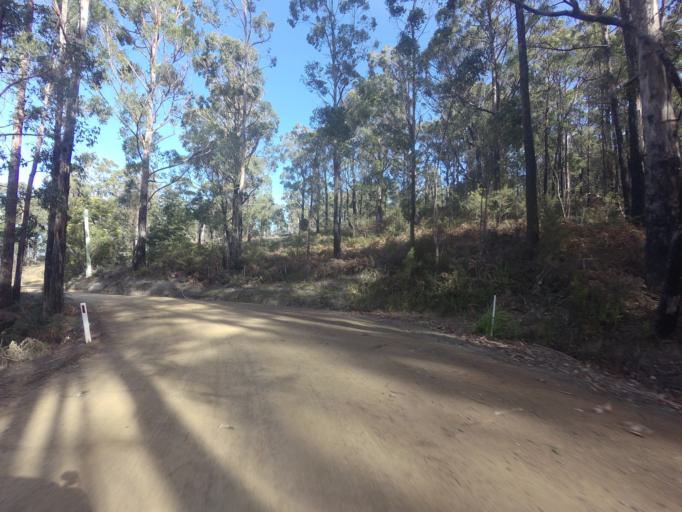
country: AU
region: Tasmania
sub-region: Kingborough
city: Kettering
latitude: -43.0958
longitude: 147.2607
